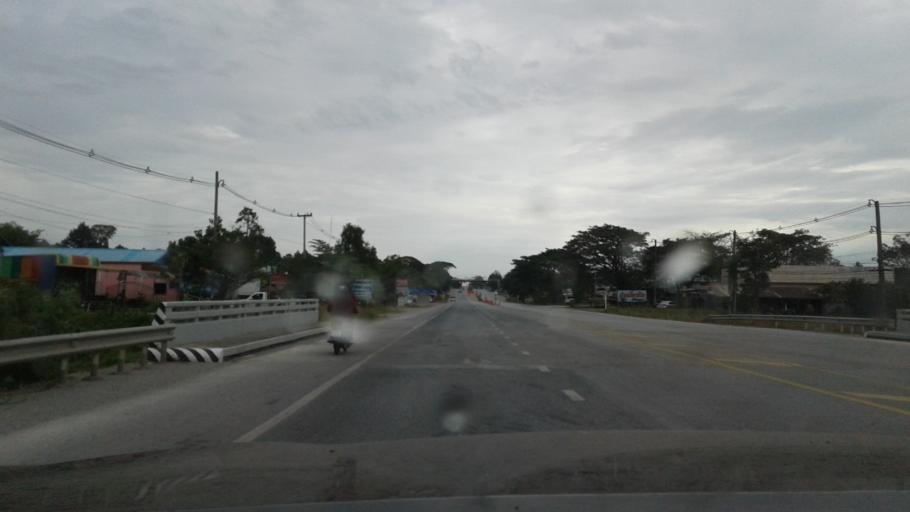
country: TH
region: Changwat Udon Thani
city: Nong Wua So
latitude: 17.2674
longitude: 102.5944
